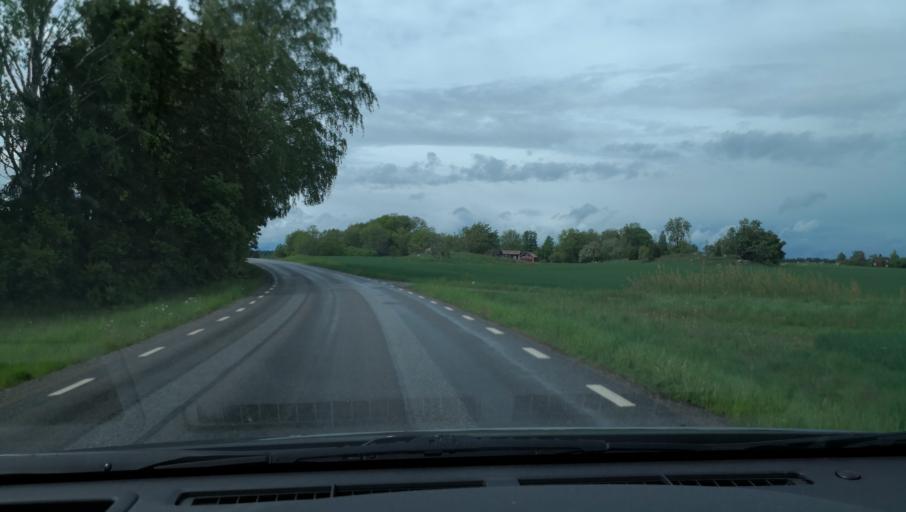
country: SE
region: Uppsala
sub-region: Enkopings Kommun
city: Orsundsbro
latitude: 59.6987
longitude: 17.3667
